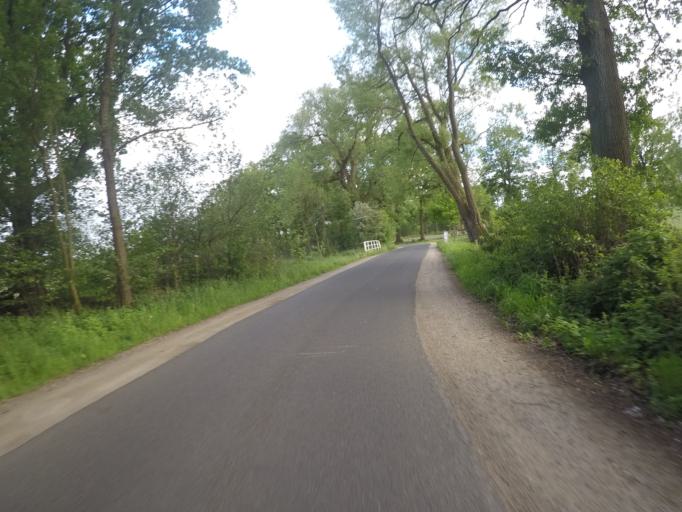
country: DE
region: Schleswig-Holstein
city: Bonningstedt
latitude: 53.6594
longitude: 9.9275
